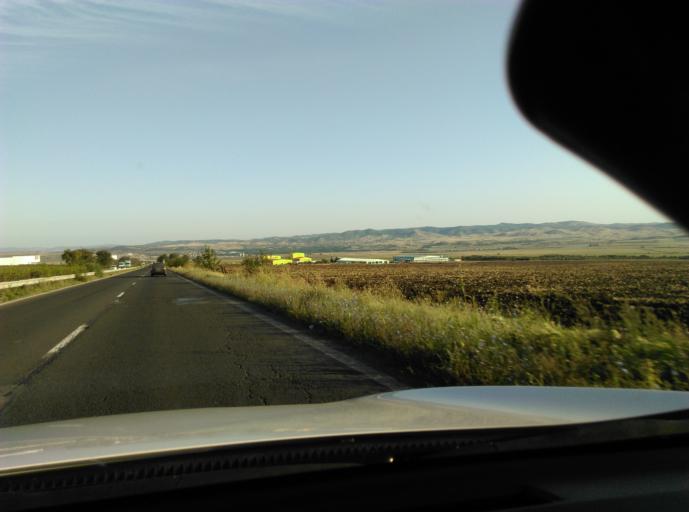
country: BG
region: Burgas
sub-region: Obshtina Burgas
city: Burgas
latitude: 42.5674
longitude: 27.4174
